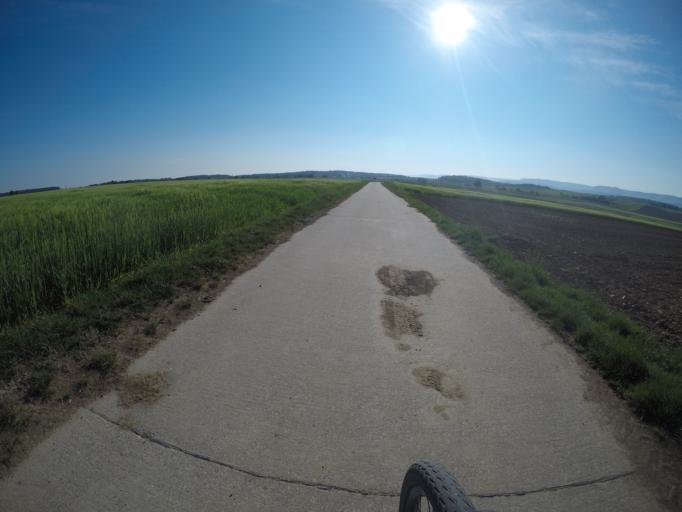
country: DE
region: Baden-Wuerttemberg
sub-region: Regierungsbezirk Stuttgart
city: Wolfschlugen
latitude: 48.6445
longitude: 9.2670
